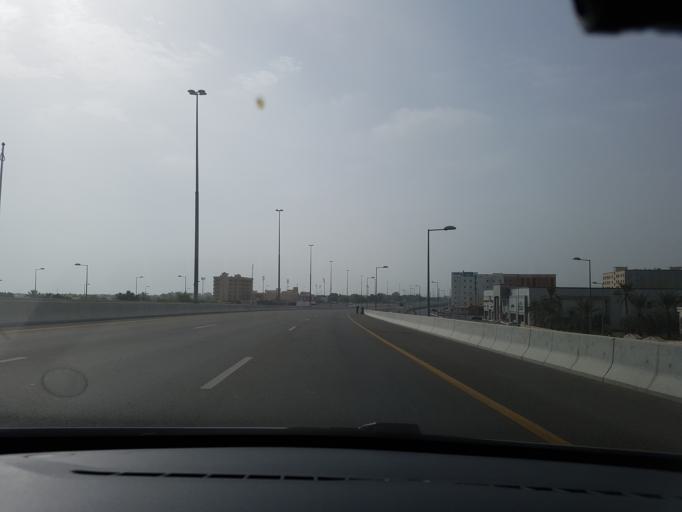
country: OM
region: Al Batinah
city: Al Sohar
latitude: 24.3406
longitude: 56.7321
